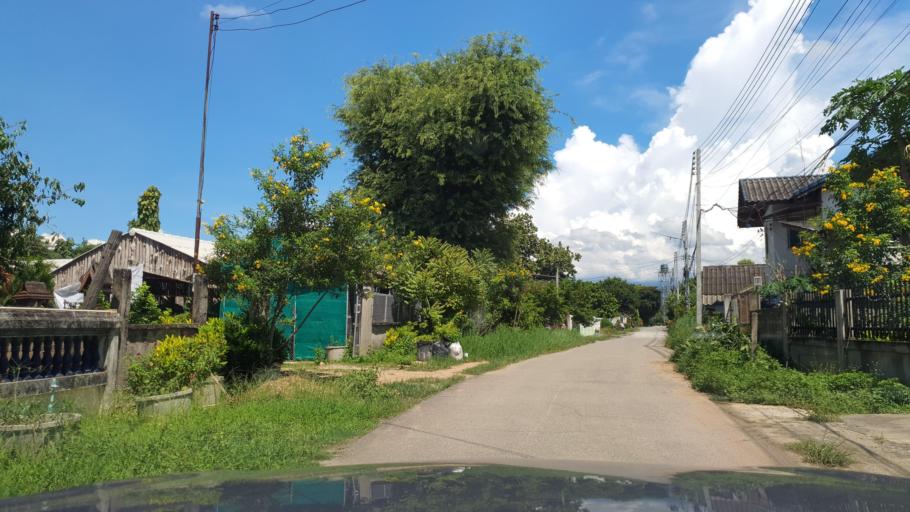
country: TH
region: Chiang Mai
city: San Kamphaeng
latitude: 18.7230
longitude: 99.1542
